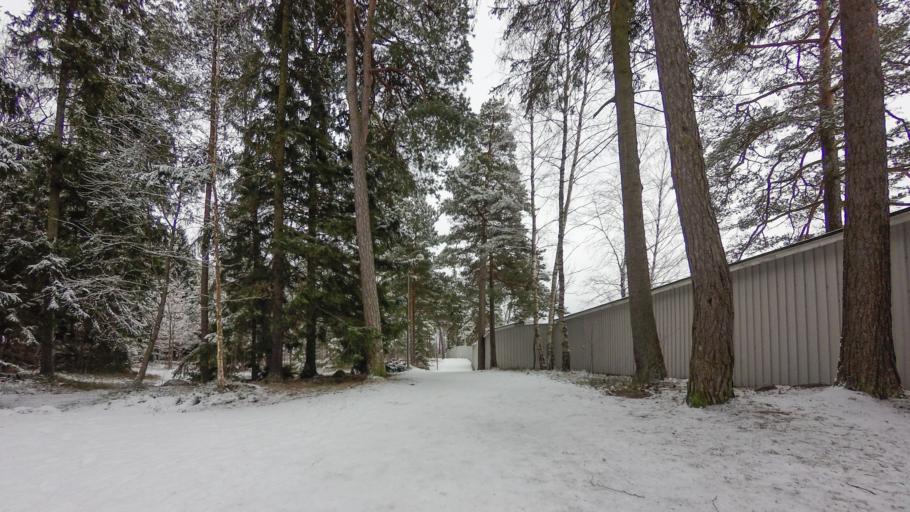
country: FI
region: Uusimaa
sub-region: Helsinki
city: Teekkarikylae
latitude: 60.1824
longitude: 24.8796
